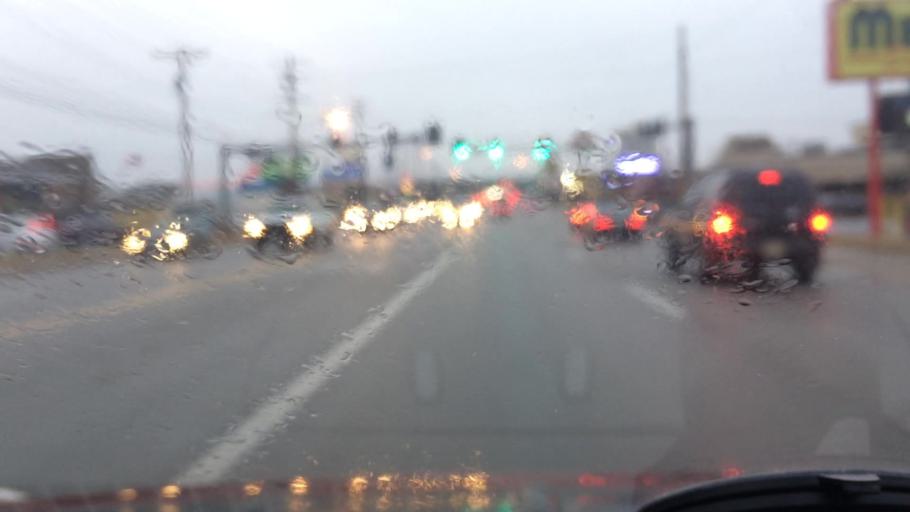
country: US
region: Missouri
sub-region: Greene County
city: Springfield
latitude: 37.1803
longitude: -93.2288
